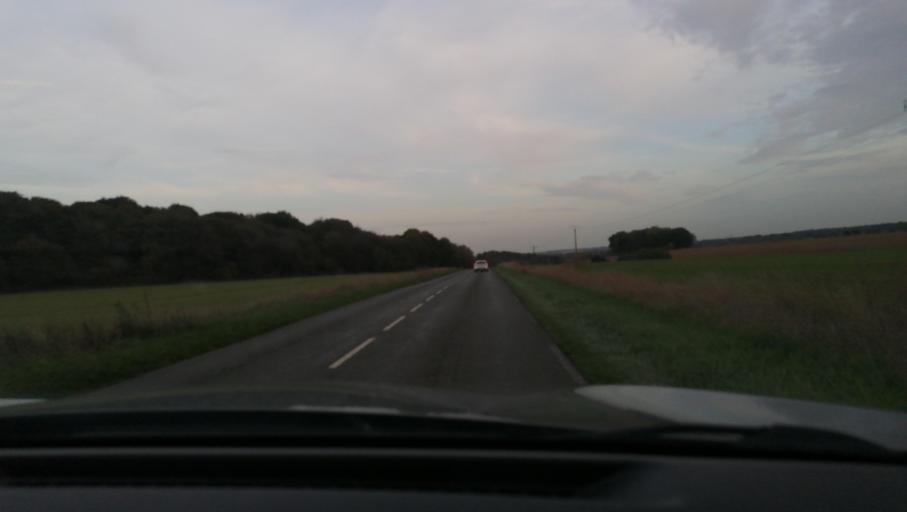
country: FR
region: Picardie
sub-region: Departement de la Somme
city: Picquigny
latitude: 49.8907
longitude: 2.1534
